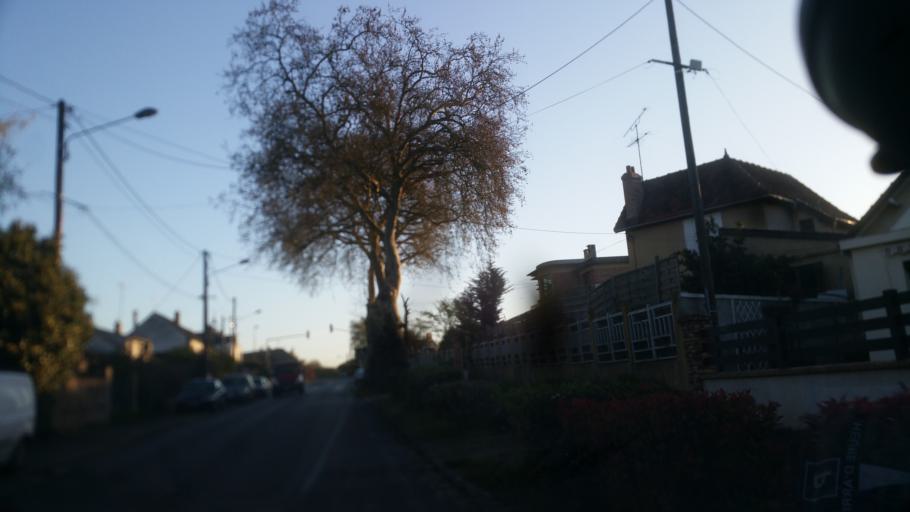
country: FR
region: Ile-de-France
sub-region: Departement de l'Essonne
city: Angervilliers
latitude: 48.5928
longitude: 2.0635
